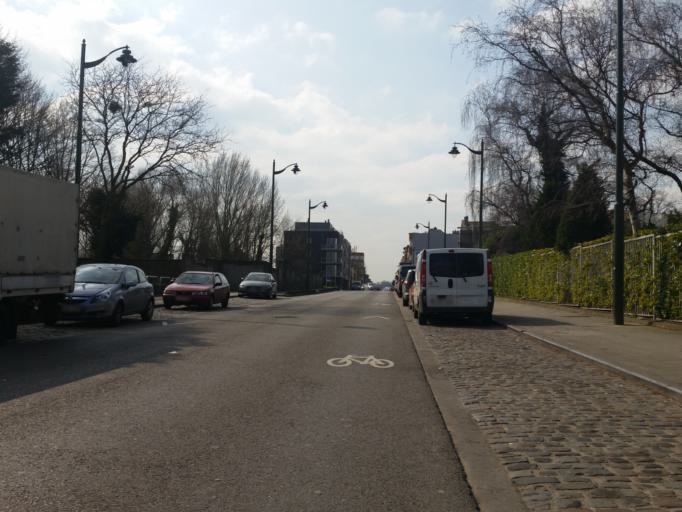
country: BE
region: Brussels Capital
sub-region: Bruxelles-Capitale
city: Brussels
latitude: 50.8434
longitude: 4.3189
